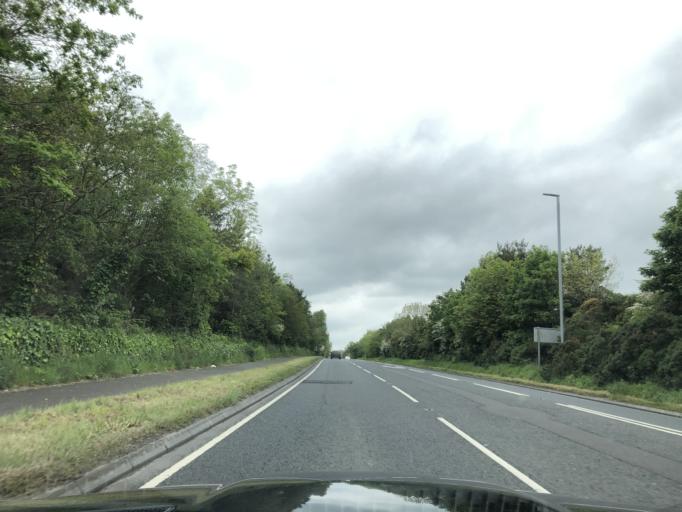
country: GB
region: Northern Ireland
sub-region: Down District
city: Downpatrick
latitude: 54.3460
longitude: -5.7341
